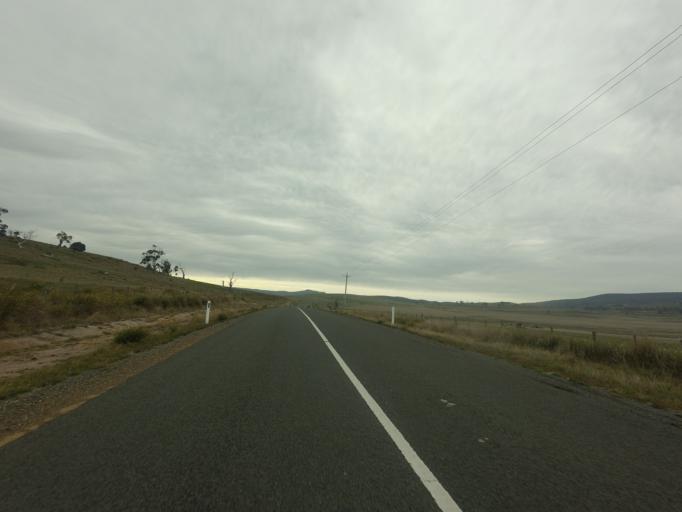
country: AU
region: Tasmania
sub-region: Derwent Valley
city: New Norfolk
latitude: -42.4340
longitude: 146.9847
